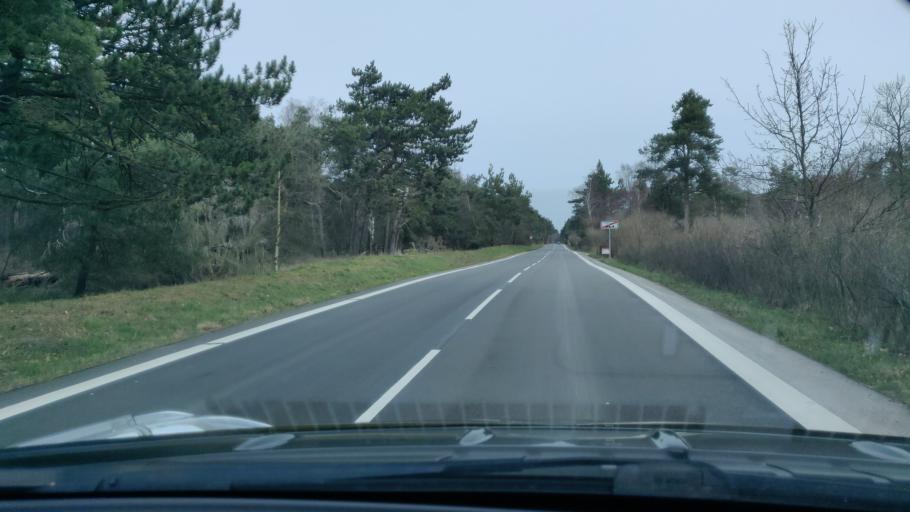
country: DK
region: Zealand
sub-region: Odsherred Kommune
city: Hojby
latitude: 55.8864
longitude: 11.5528
